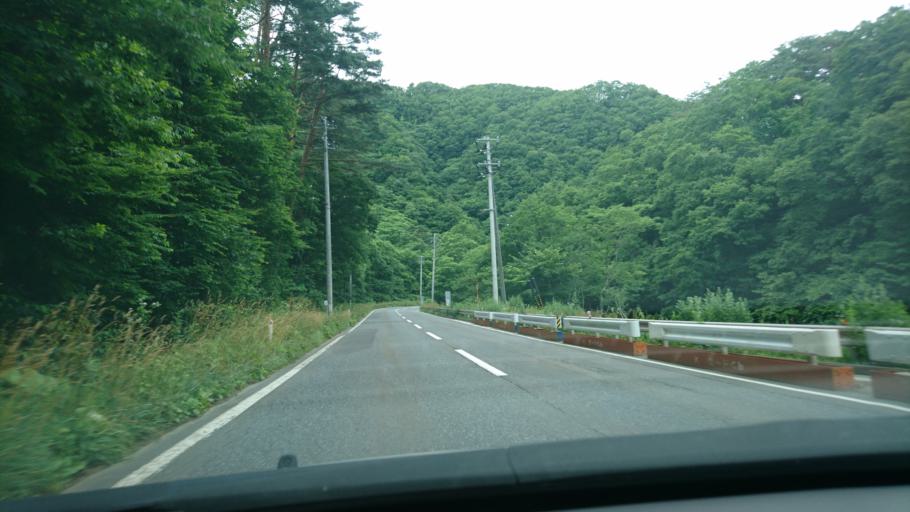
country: JP
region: Iwate
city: Miyako
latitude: 39.9864
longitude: 141.8639
